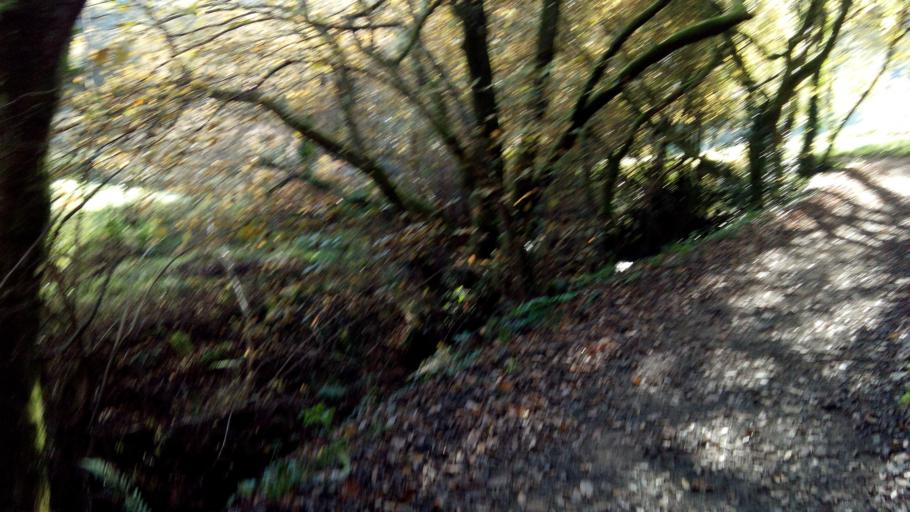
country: ES
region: Galicia
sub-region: Provincia de Pontevedra
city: Meis
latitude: 42.4778
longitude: -8.7418
